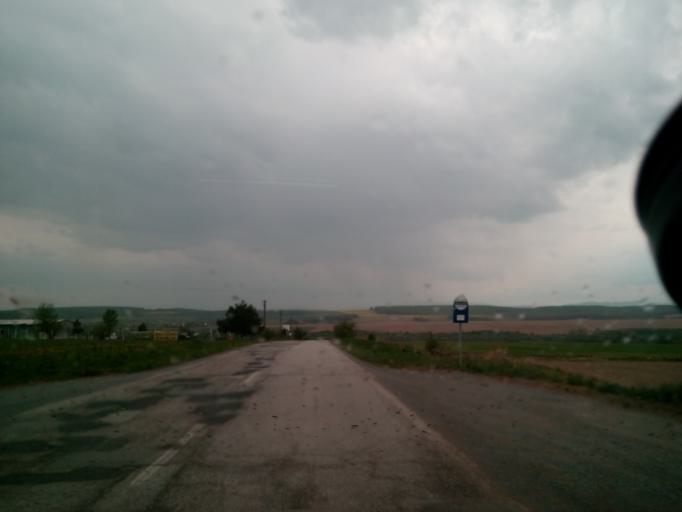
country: SK
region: Kosicky
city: Kosice
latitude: 48.7467
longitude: 21.4480
